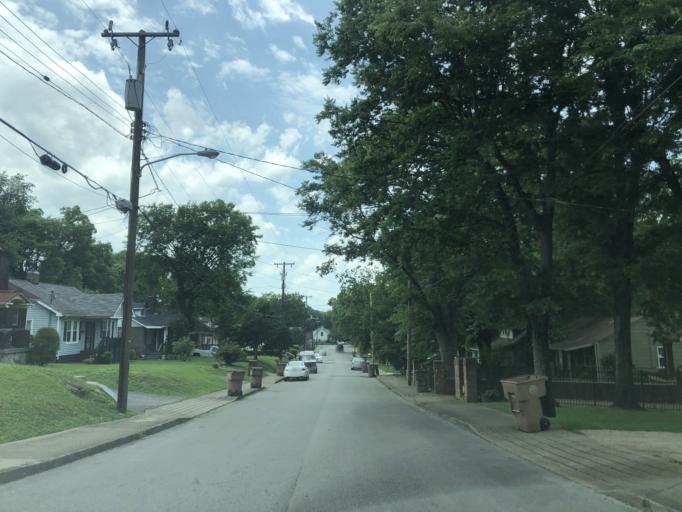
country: US
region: Tennessee
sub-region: Davidson County
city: Nashville
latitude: 36.1871
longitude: -86.7516
